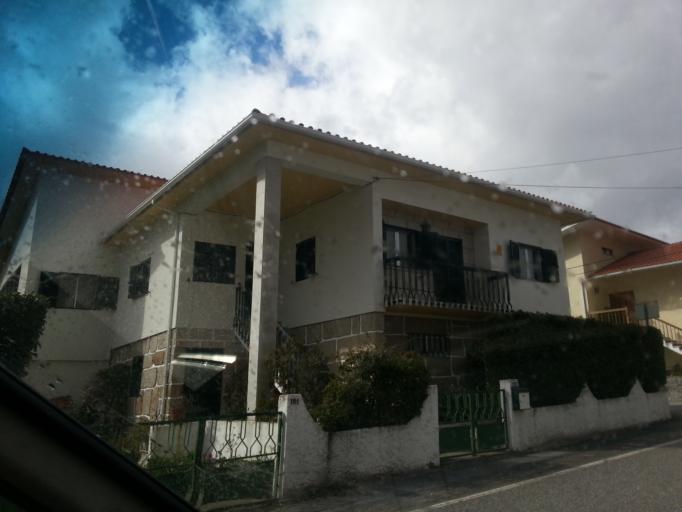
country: PT
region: Viseu
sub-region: Viseu
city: Rio de Loba
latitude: 40.6395
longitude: -7.8663
